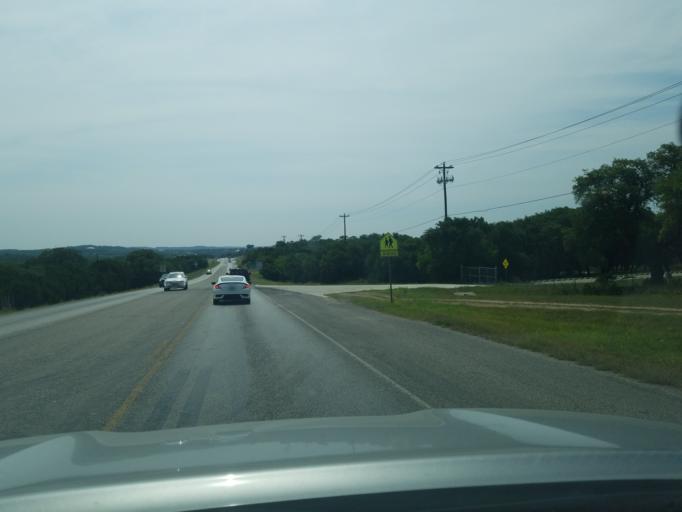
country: US
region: Texas
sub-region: Comal County
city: Bulverde
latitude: 29.7996
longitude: -98.4370
